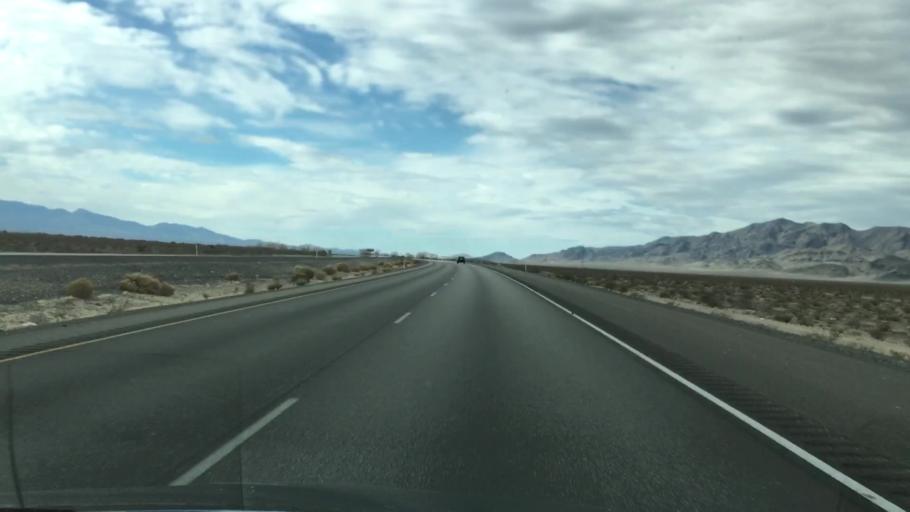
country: US
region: Nevada
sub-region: Nye County
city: Pahrump
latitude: 36.5794
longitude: -115.7051
